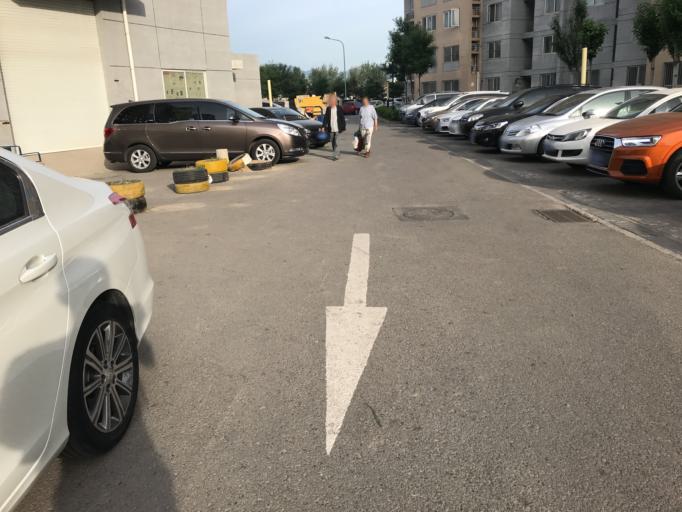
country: CN
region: Beijing
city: Shahe
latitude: 40.1222
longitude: 116.2083
